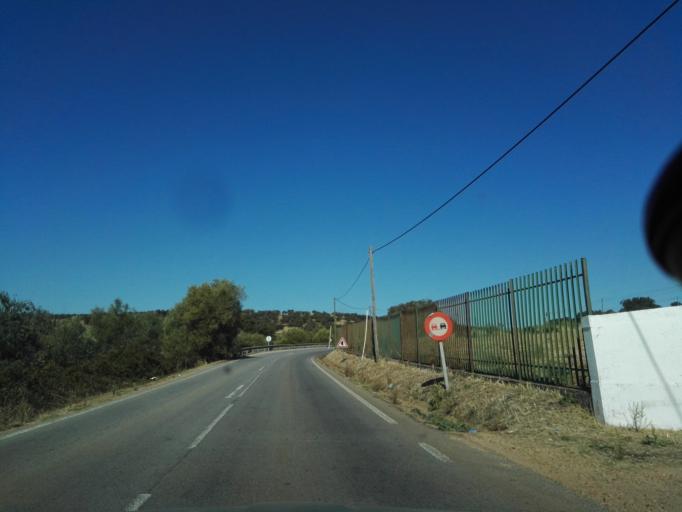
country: PT
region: Portalegre
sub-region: Elvas
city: Elvas
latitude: 38.9008
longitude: -7.1789
